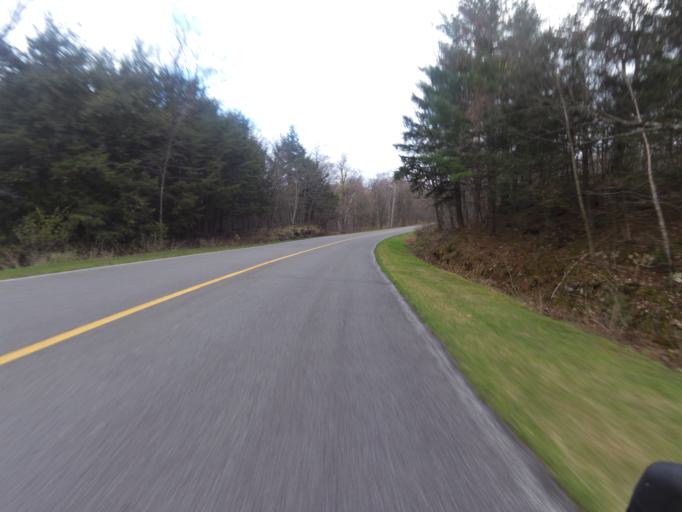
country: CA
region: Quebec
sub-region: Outaouais
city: Wakefield
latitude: 45.5010
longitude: -75.8750
